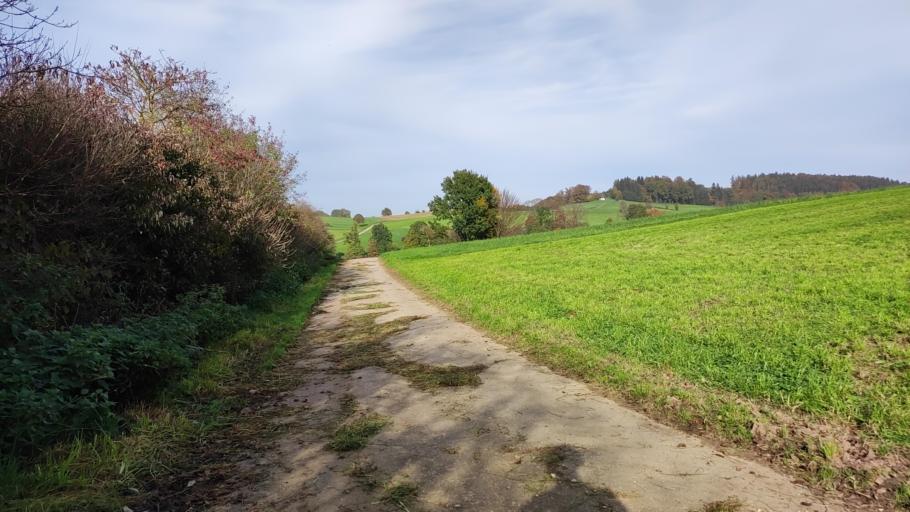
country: DE
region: Bavaria
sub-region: Swabia
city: Ziemetshausen
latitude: 48.2813
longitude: 10.5505
